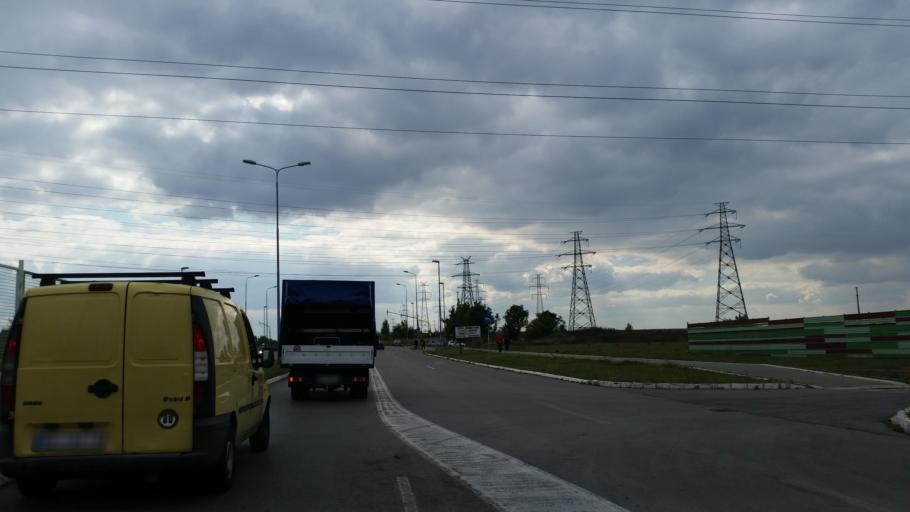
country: RS
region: Central Serbia
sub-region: Belgrade
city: Zemun
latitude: 44.8243
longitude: 20.3616
